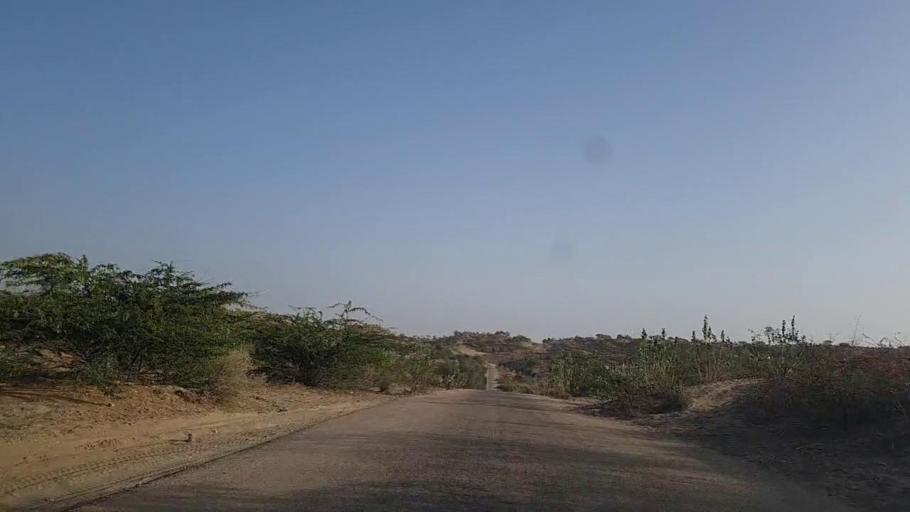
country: PK
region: Sindh
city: Diplo
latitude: 24.6044
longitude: 69.3797
